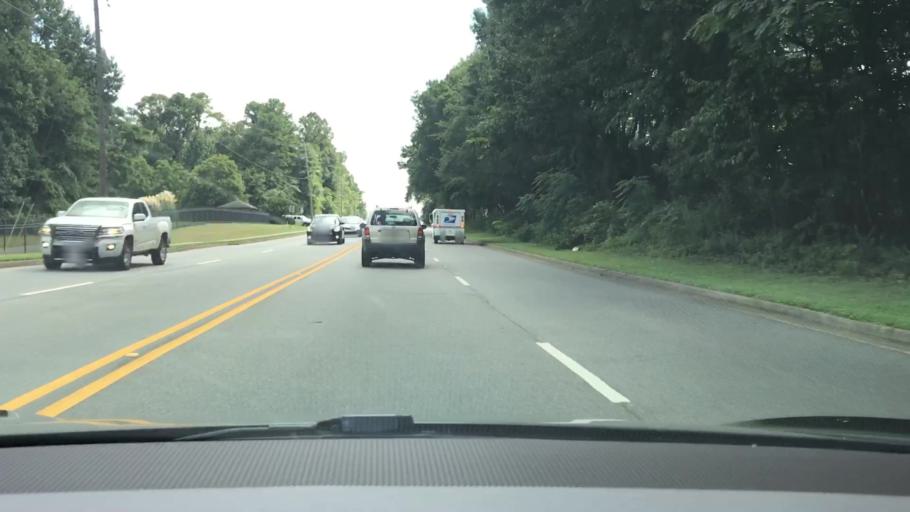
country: US
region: Alabama
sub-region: Lee County
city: Auburn
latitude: 32.6206
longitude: -85.4476
